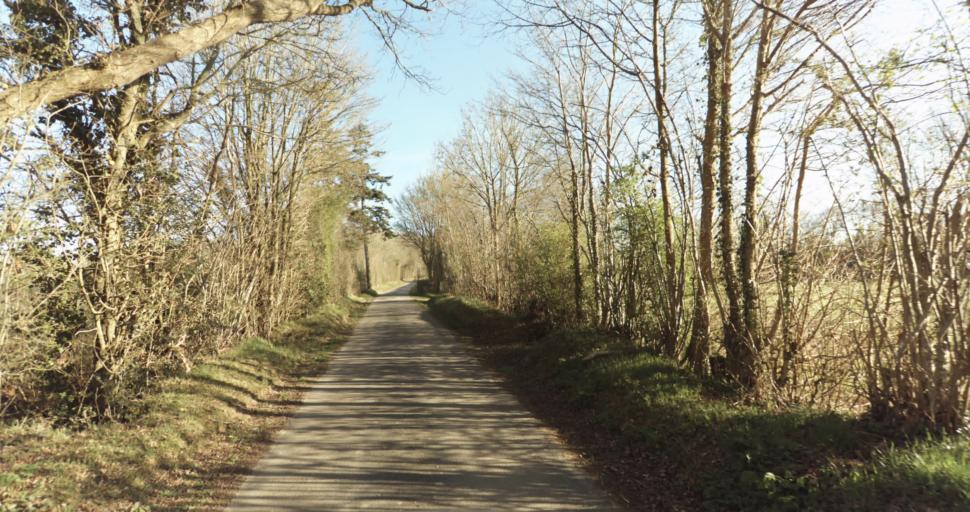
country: FR
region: Lower Normandy
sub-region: Departement du Calvados
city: Livarot
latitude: 48.9871
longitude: 0.0849
